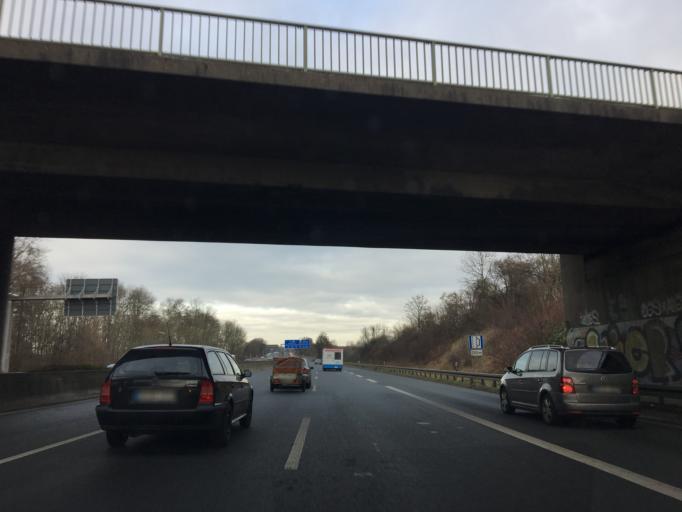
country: DE
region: North Rhine-Westphalia
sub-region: Regierungsbezirk Koln
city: Bonn
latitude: 50.7530
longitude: 7.1415
